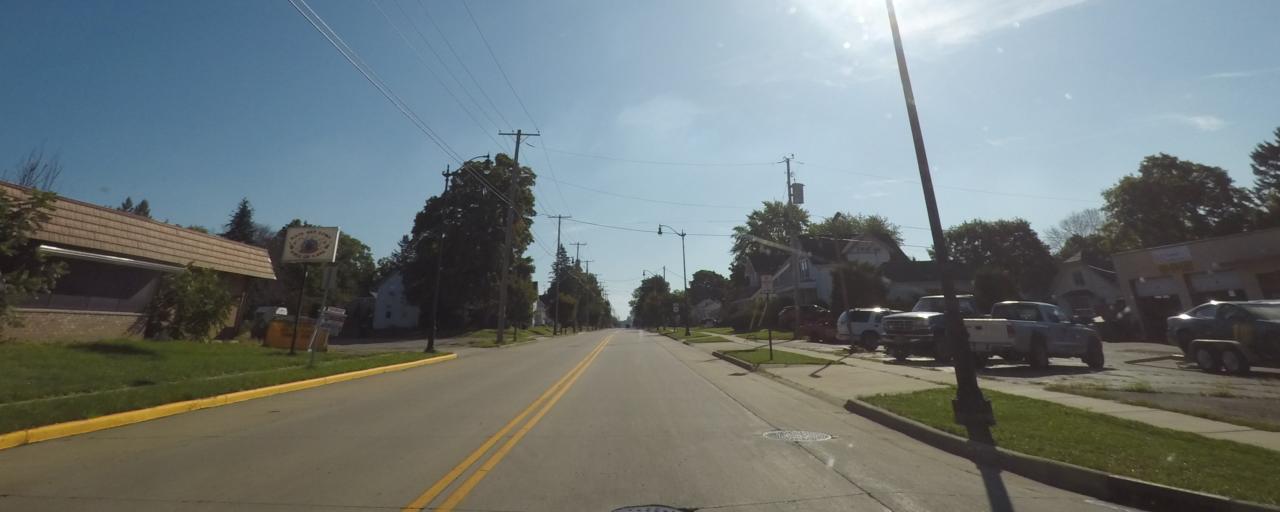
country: US
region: Wisconsin
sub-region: Jefferson County
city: Jefferson
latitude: 43.0050
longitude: -88.7977
